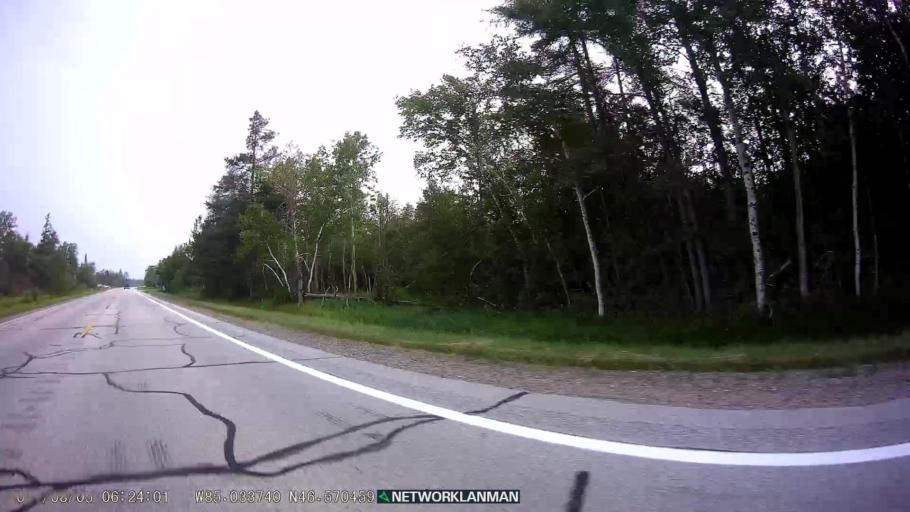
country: US
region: Michigan
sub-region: Luce County
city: Newberry
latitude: 46.5702
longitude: -85.0340
